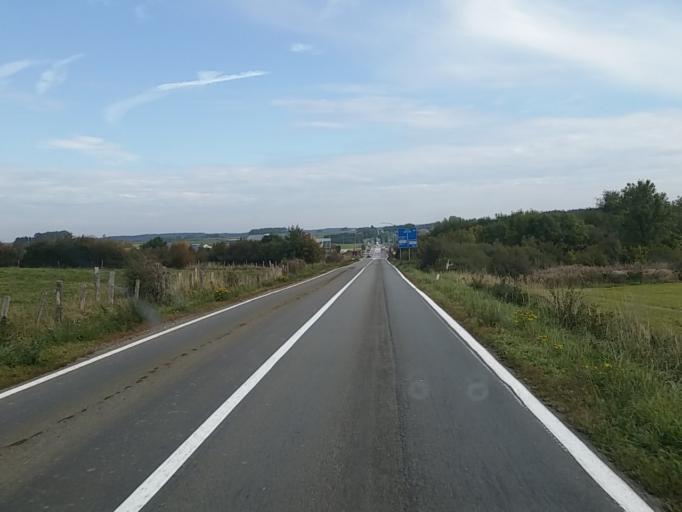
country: BE
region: Wallonia
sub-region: Province du Luxembourg
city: Habay-la-Vieille
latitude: 49.7007
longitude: 5.6208
